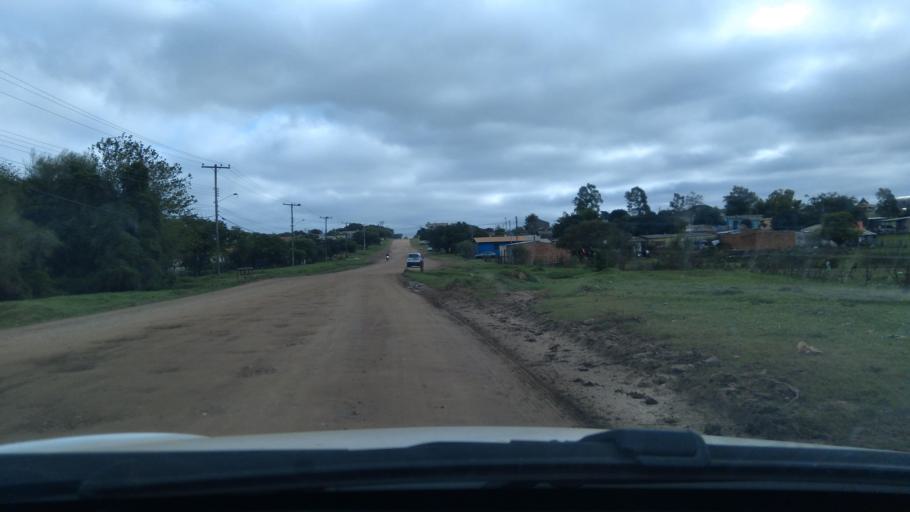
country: BR
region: Rio Grande do Sul
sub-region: Dom Pedrito
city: Dom Pedrito
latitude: -30.9816
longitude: -54.6530
